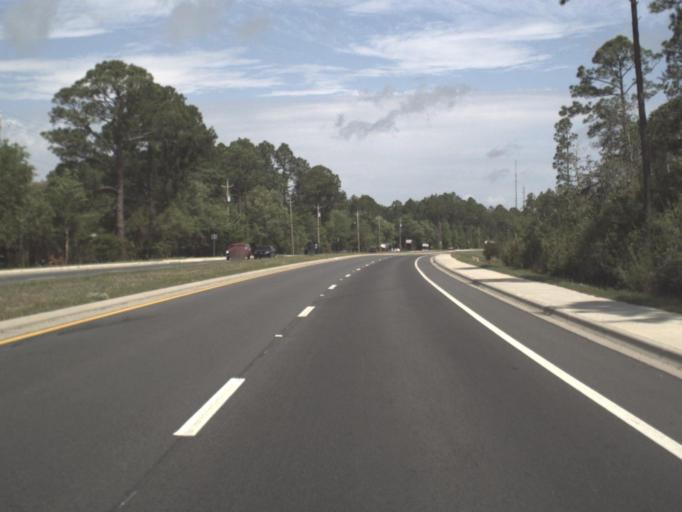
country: US
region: Florida
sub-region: Santa Rosa County
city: Holley
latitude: 30.4545
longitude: -86.9086
